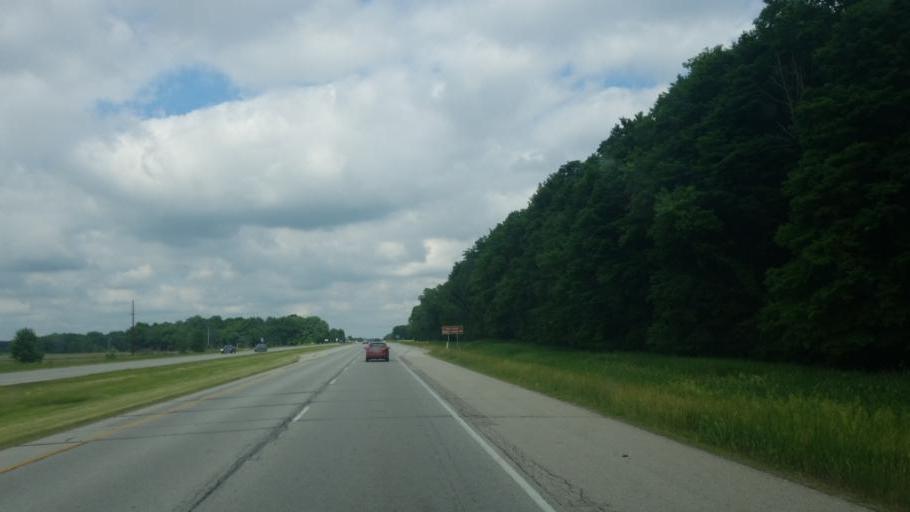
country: US
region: Indiana
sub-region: Kosciusko County
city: Warsaw
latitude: 41.2693
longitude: -85.9150
